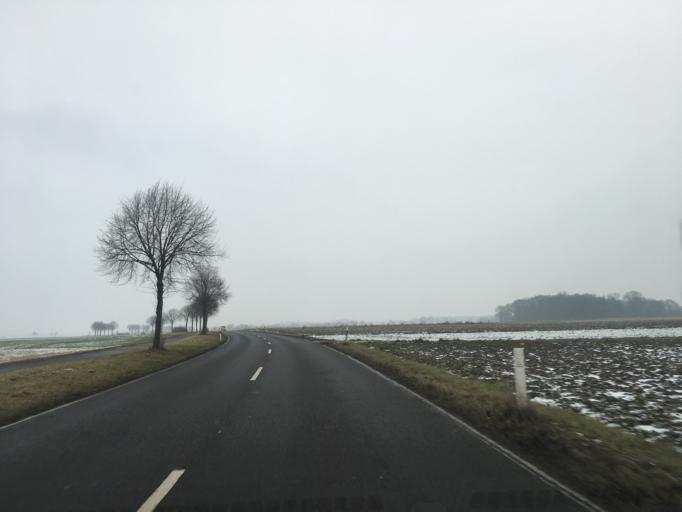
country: DE
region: North Rhine-Westphalia
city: Huckelhoven
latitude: 51.1082
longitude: 6.2405
